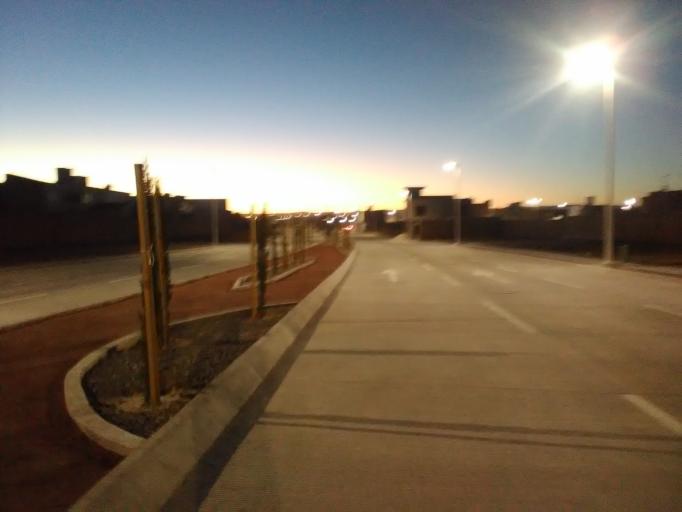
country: MX
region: Durango
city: Victoria de Durango
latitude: 23.9999
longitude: -104.6319
